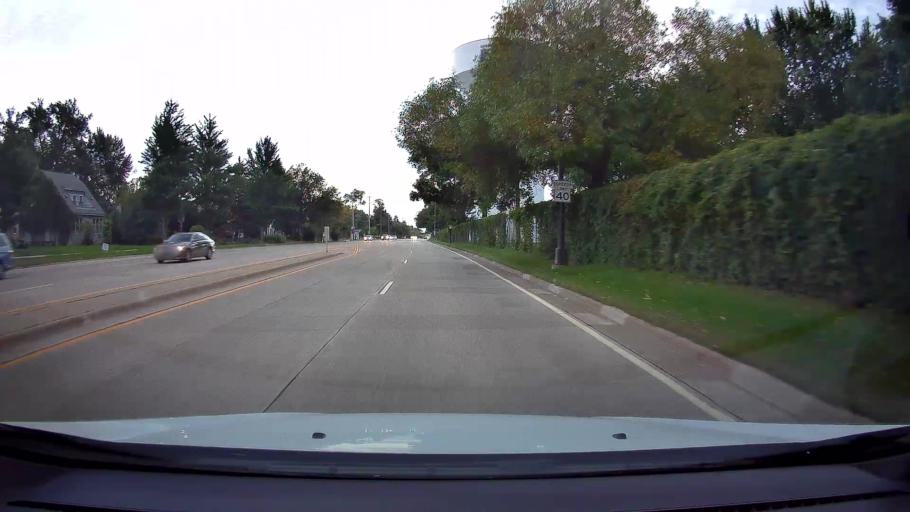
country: US
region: Minnesota
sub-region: Ramsey County
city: Falcon Heights
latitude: 44.9877
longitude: -93.1671
